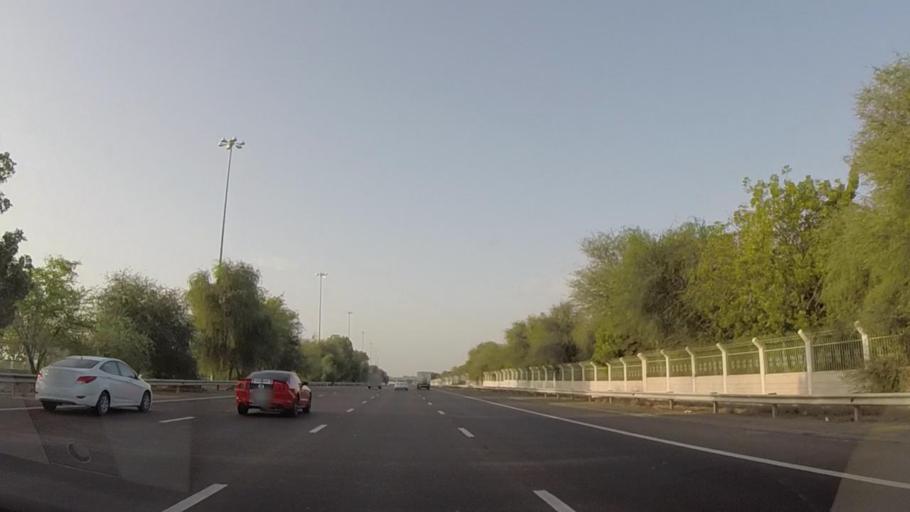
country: AE
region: Dubai
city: Dubai
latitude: 24.8191
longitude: 54.8746
